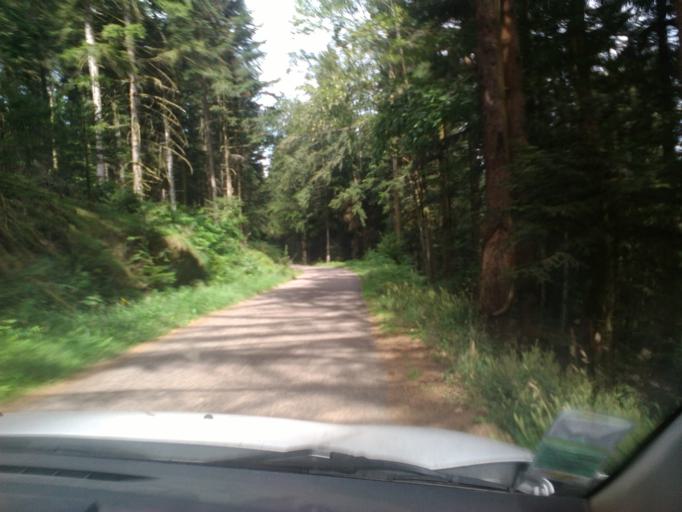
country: FR
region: Lorraine
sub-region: Departement des Vosges
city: Le Tholy
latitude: 48.1135
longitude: 6.7270
